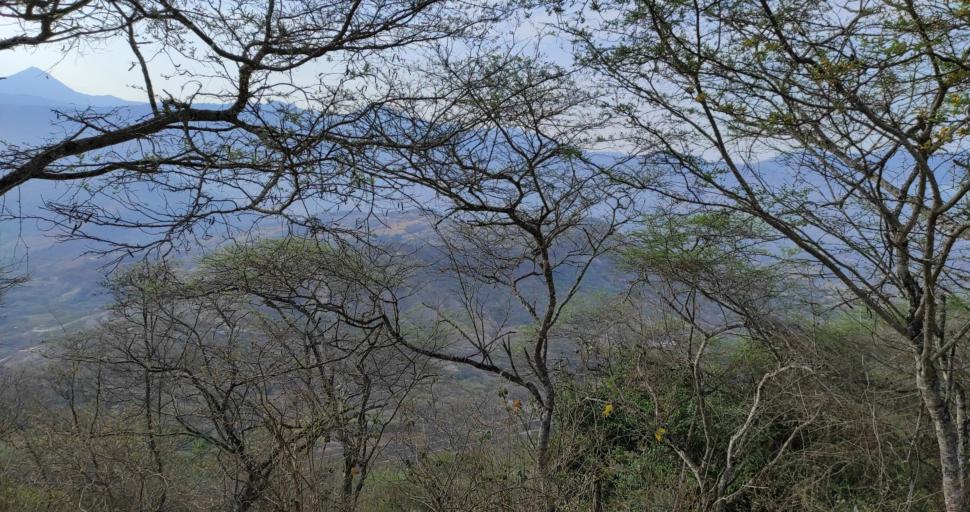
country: EC
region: Loja
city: Catacocha
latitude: -3.9853
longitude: -79.6868
